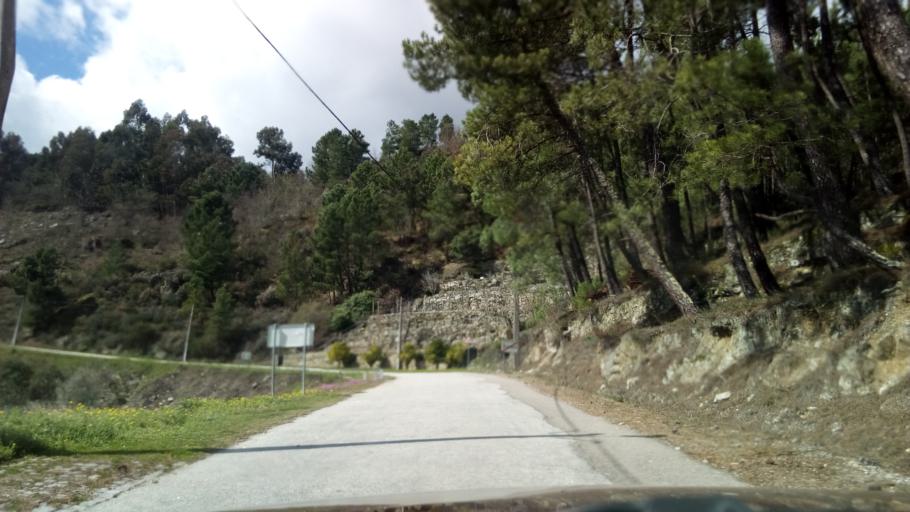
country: PT
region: Guarda
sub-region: Fornos de Algodres
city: Fornos de Algodres
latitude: 40.6620
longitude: -7.4981
